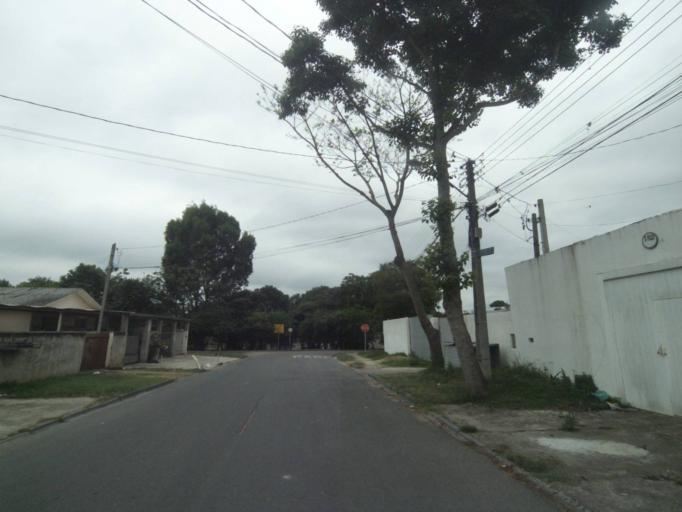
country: BR
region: Parana
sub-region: Sao Jose Dos Pinhais
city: Sao Jose dos Pinhais
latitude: -25.5360
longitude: -49.2519
